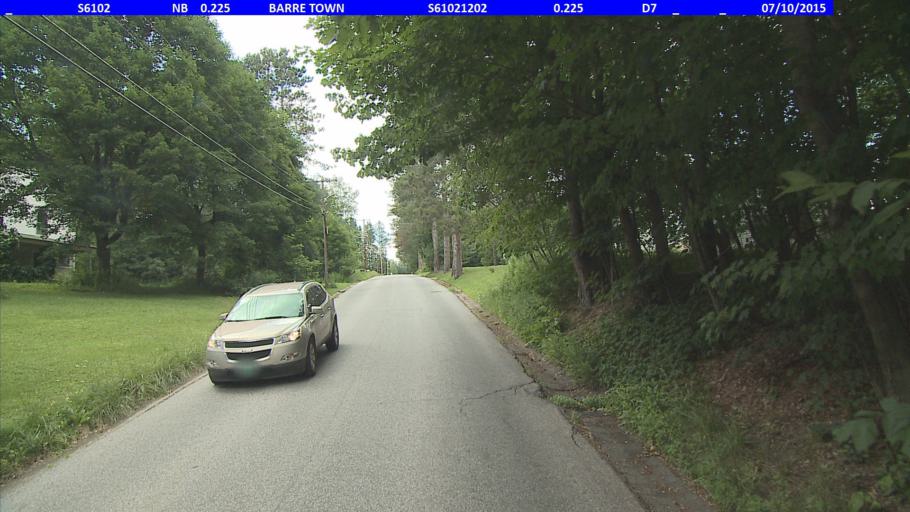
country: US
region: Vermont
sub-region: Washington County
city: Barre
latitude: 44.2159
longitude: -72.5092
